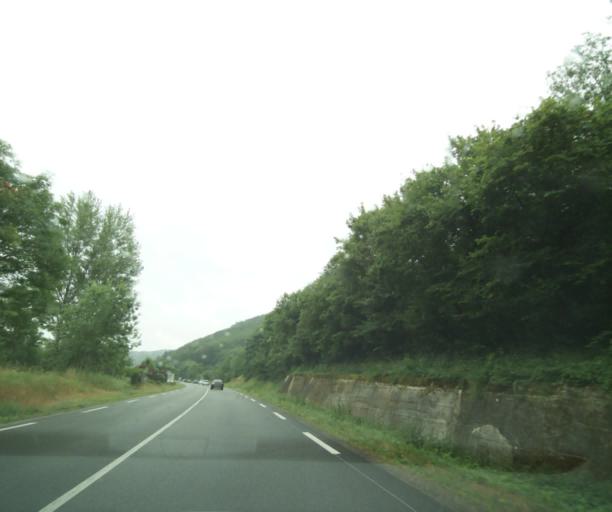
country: FR
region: Midi-Pyrenees
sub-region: Departement de l'Aveyron
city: Laissac
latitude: 44.3961
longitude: 2.7525
